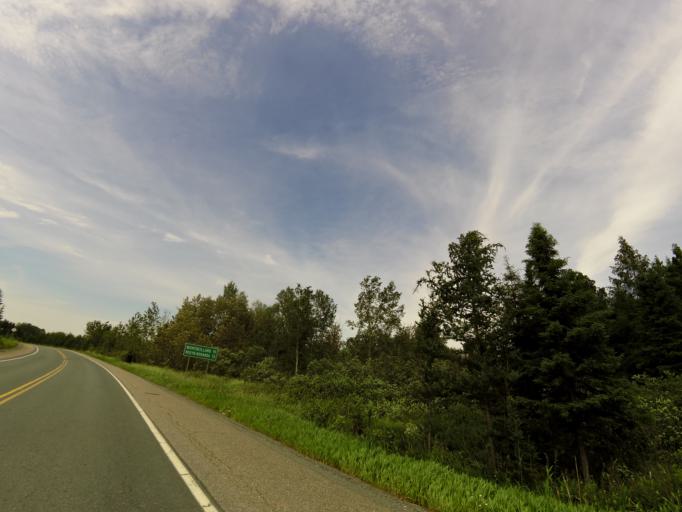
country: CA
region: Quebec
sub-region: Abitibi-Temiscamingue
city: Rouyn-Noranda
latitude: 47.9182
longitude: -79.2405
